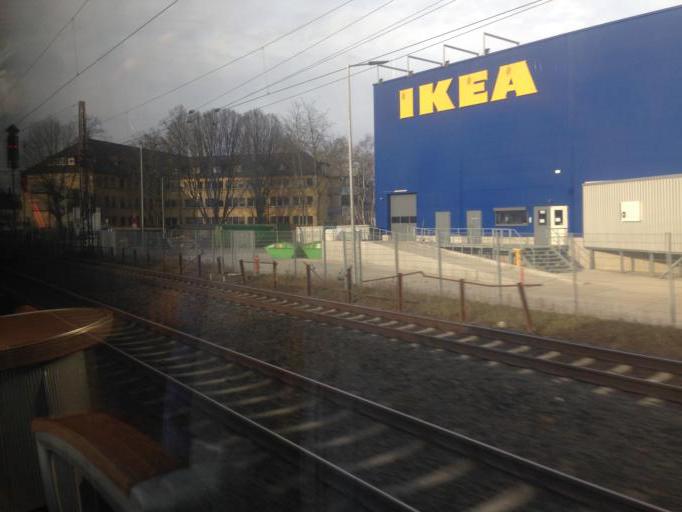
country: DE
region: Hesse
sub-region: Regierungsbezirk Giessen
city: Wetzlar
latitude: 50.5690
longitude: 8.4953
